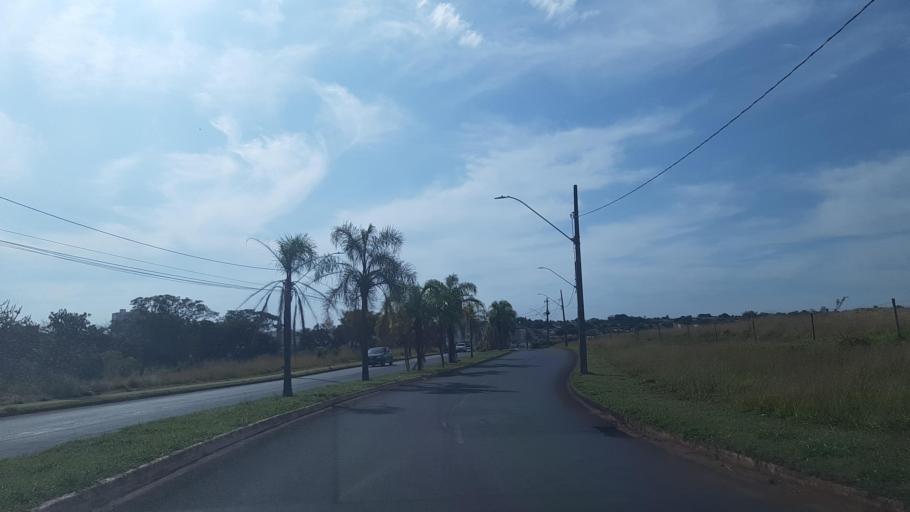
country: BR
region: Minas Gerais
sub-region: Uberlandia
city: Uberlandia
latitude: -18.8791
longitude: -48.2416
